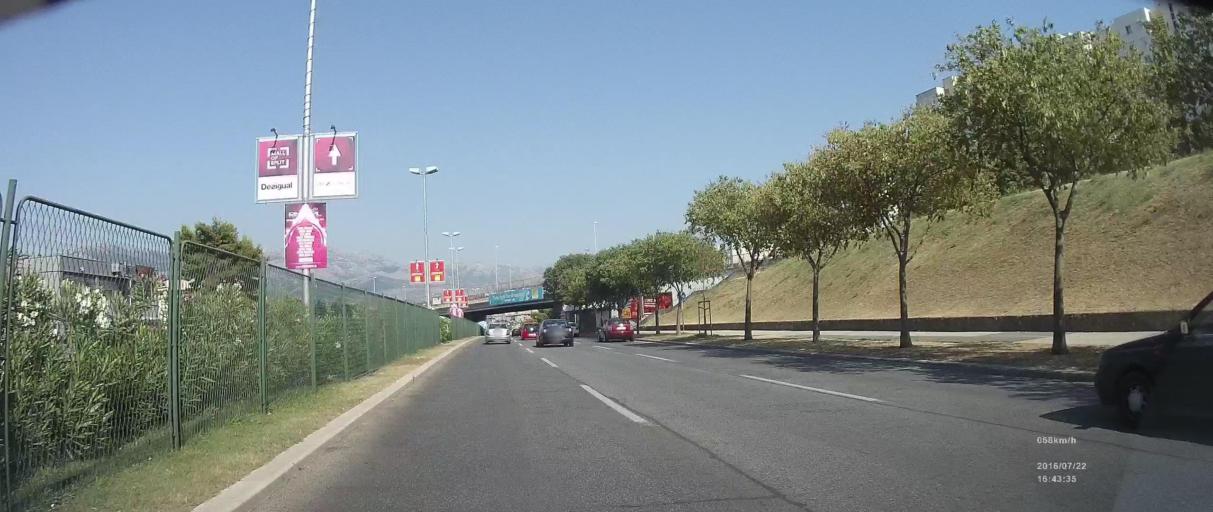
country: HR
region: Splitsko-Dalmatinska
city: Vranjic
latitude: 43.5193
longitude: 16.4716
